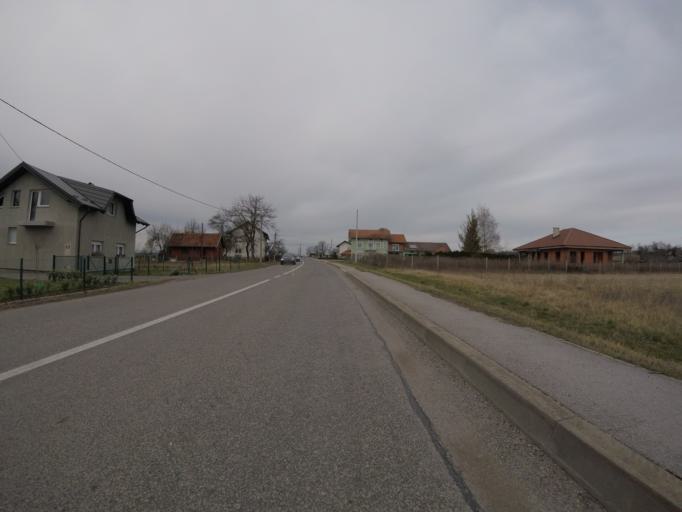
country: HR
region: Grad Zagreb
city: Horvati
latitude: 45.5775
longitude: 15.8607
